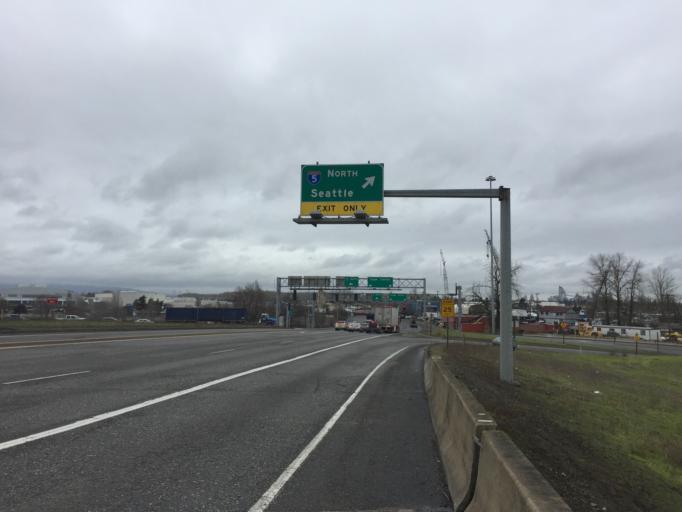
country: US
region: Washington
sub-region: Clark County
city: Vancouver
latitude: 45.6047
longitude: -122.6832
